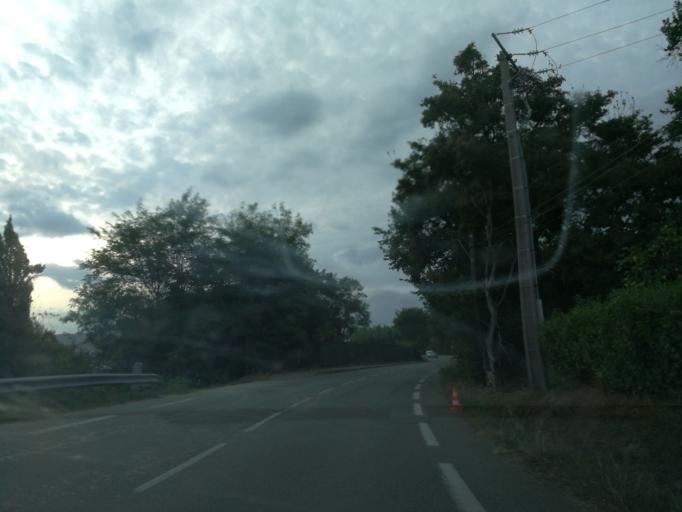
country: FR
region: Midi-Pyrenees
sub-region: Departement de la Haute-Garonne
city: Balma
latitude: 43.6113
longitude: 1.5297
